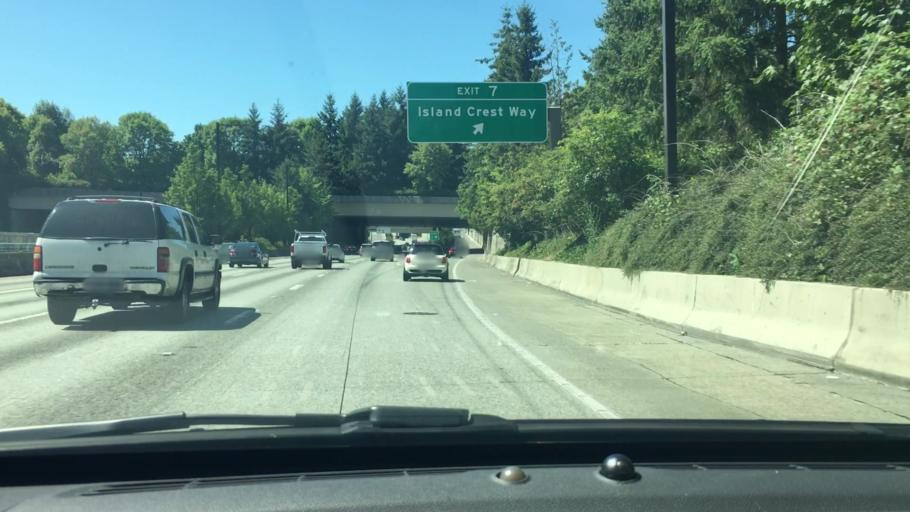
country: US
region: Washington
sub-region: King County
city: Mercer Island
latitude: 47.5848
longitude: -122.2250
